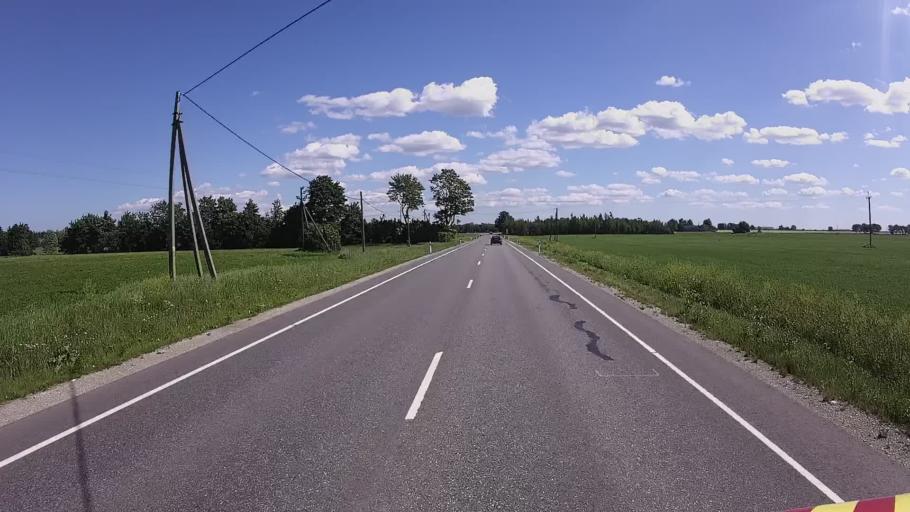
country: EE
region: Ida-Virumaa
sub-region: Johvi vald
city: Johvi
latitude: 59.3468
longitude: 27.3563
